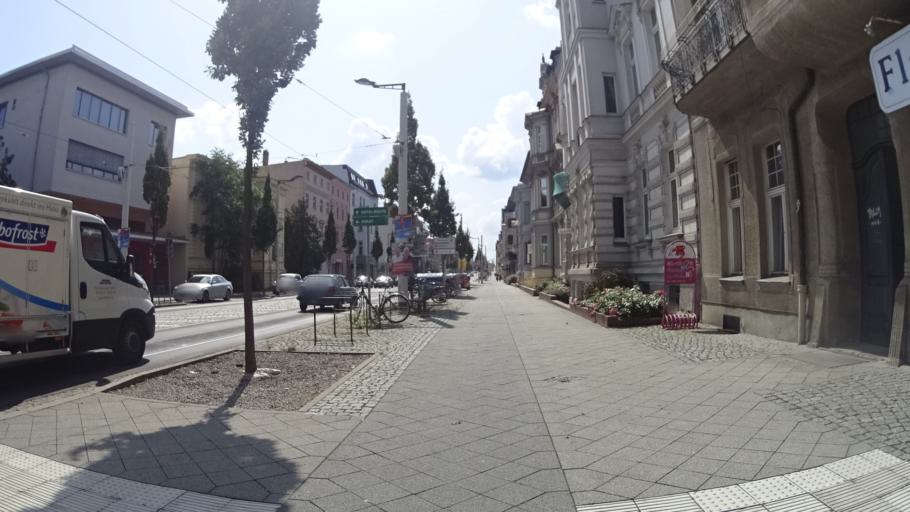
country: DE
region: Brandenburg
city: Cottbus
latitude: 51.7581
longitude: 14.3278
